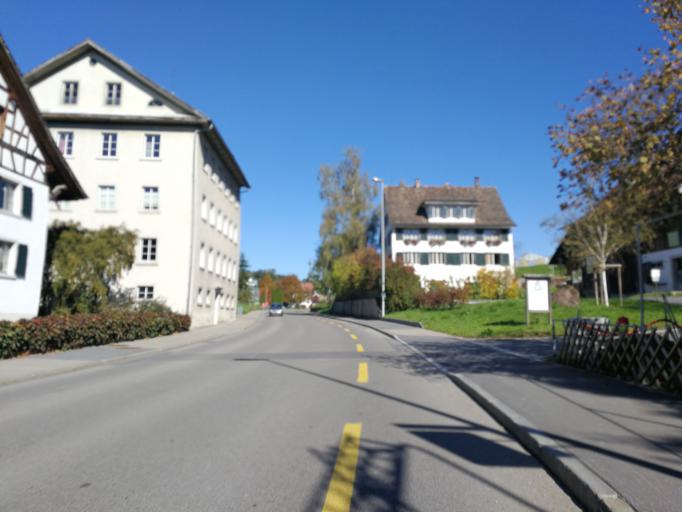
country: CH
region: Zurich
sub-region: Bezirk Hinwil
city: Gruet
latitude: 47.2939
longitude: 8.7779
